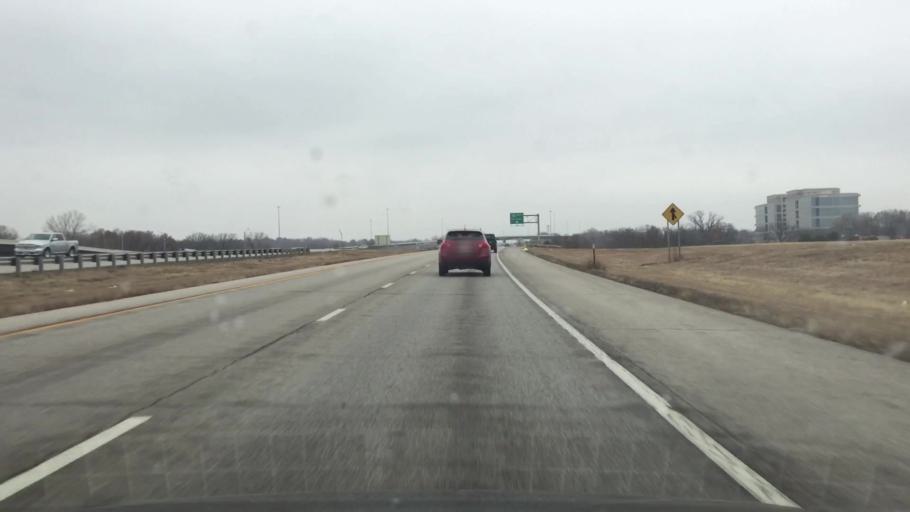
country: US
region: Kansas
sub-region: Johnson County
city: Lenexa
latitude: 38.9250
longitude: -94.7047
